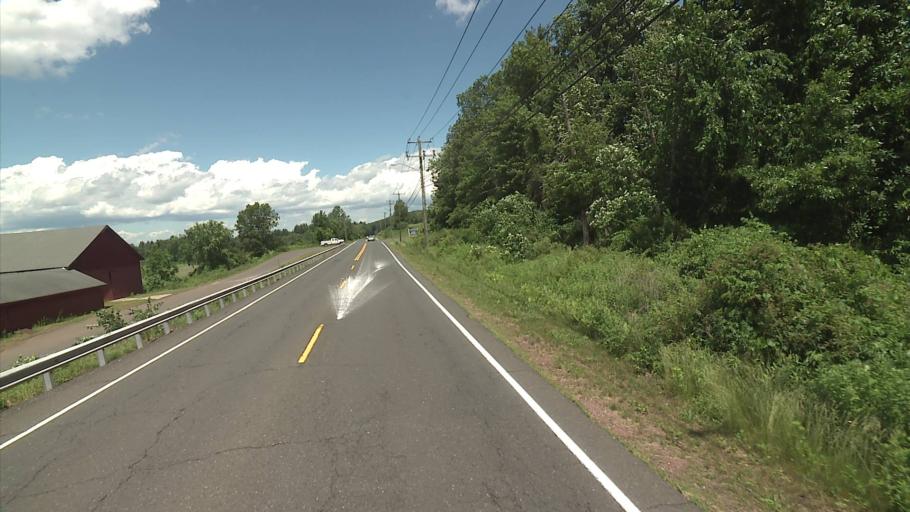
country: US
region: Massachusetts
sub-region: Hampden County
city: East Longmeadow
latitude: 42.0218
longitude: -72.5147
